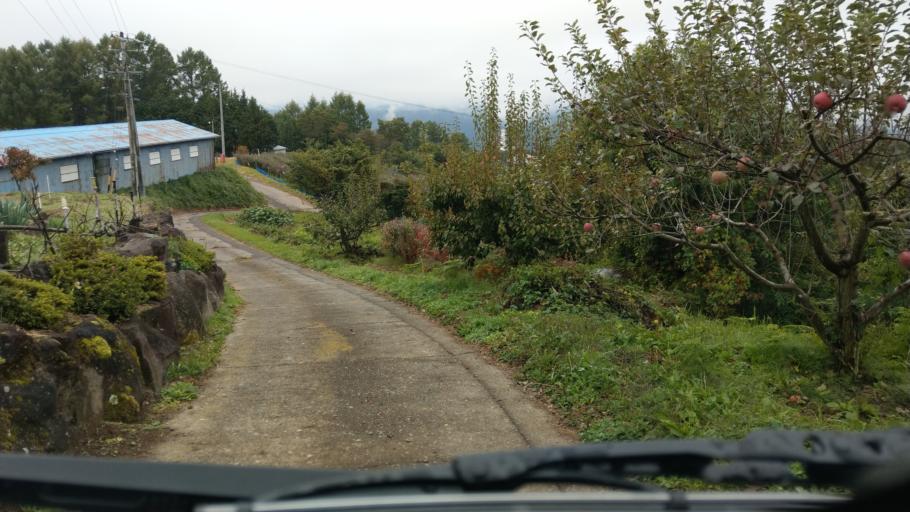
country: JP
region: Nagano
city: Komoro
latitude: 36.3574
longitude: 138.4444
